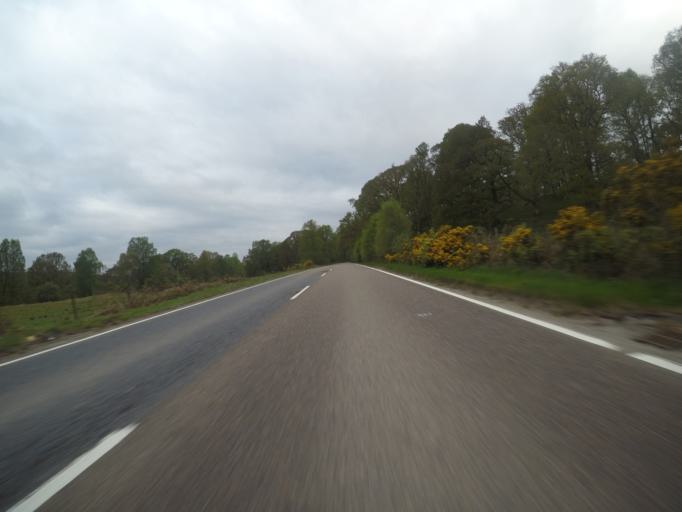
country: GB
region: Scotland
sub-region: Highland
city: Spean Bridge
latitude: 56.8936
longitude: -4.8873
